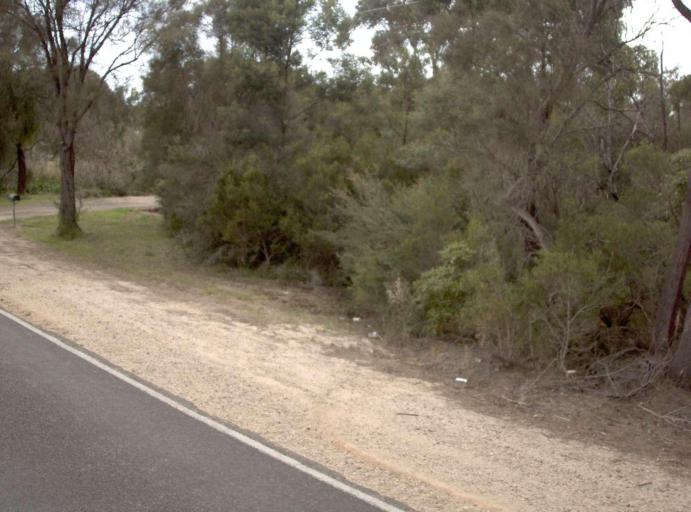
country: AU
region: Victoria
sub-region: Wellington
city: Sale
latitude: -38.1915
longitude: 147.0937
